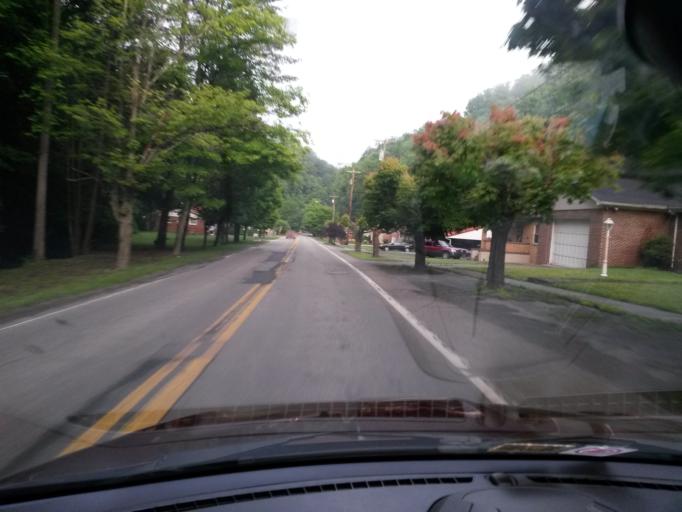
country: US
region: West Virginia
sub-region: McDowell County
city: Welch
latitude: 37.4481
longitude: -81.5574
